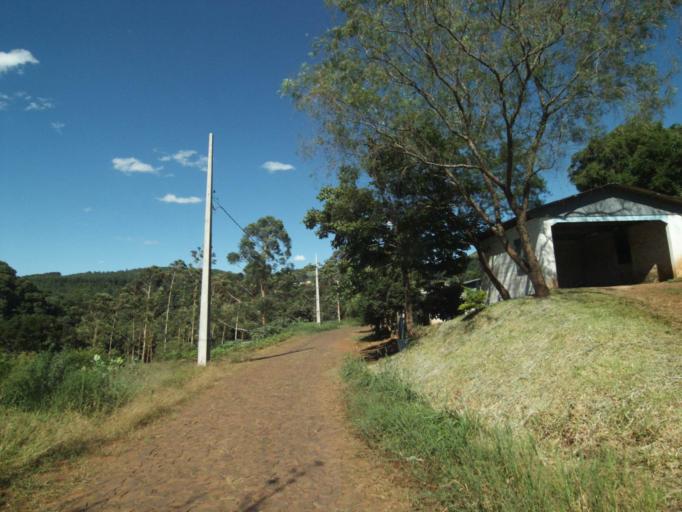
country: BR
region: Parana
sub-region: Ampere
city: Ampere
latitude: -26.1690
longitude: -53.3676
